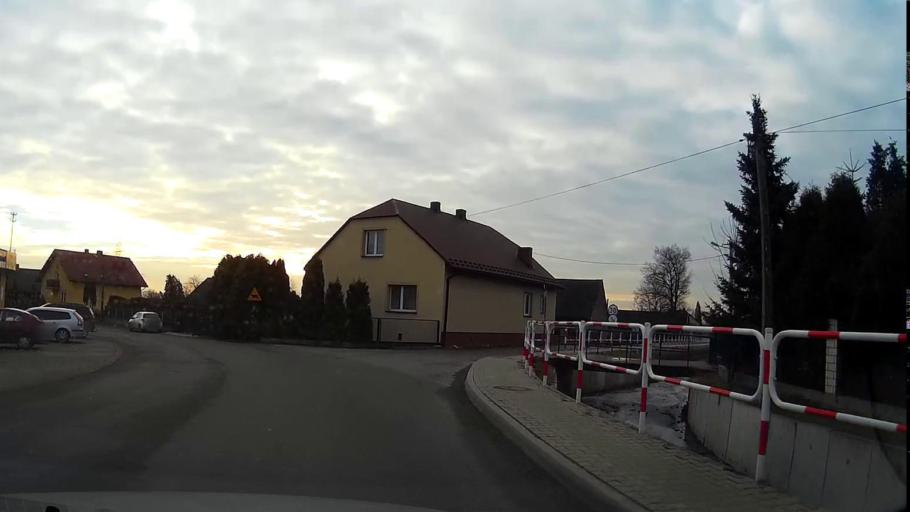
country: PL
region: Lesser Poland Voivodeship
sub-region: Powiat chrzanowski
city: Kwaczala
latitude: 50.0633
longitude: 19.4918
